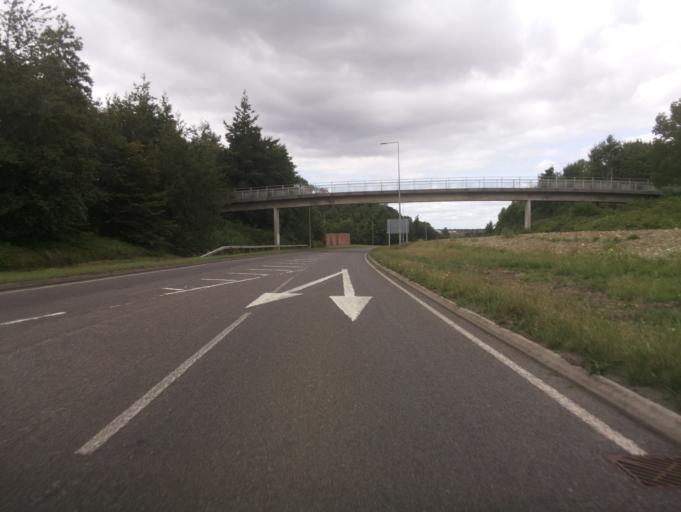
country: GB
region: England
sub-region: Milton Keynes
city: Shenley Church End
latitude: 52.0187
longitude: -0.7926
